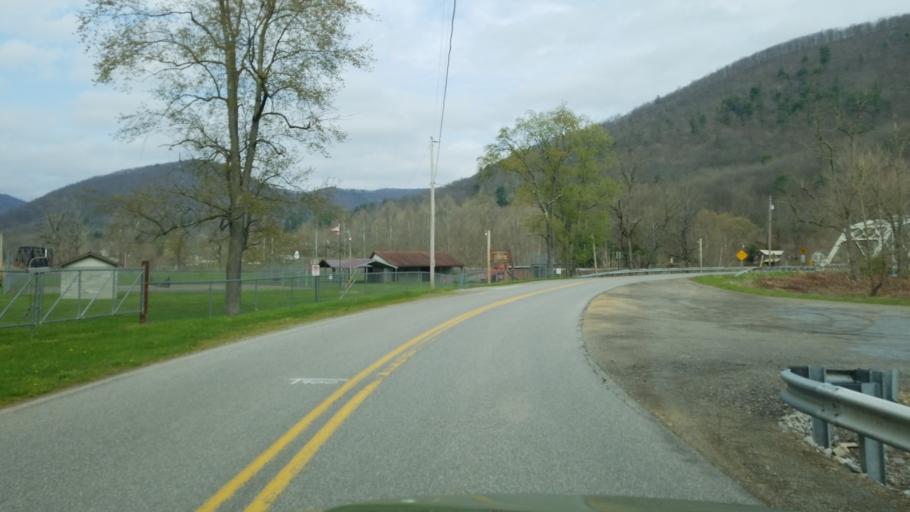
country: US
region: Pennsylvania
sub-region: Cameron County
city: Emporium
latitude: 41.3174
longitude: -78.0833
